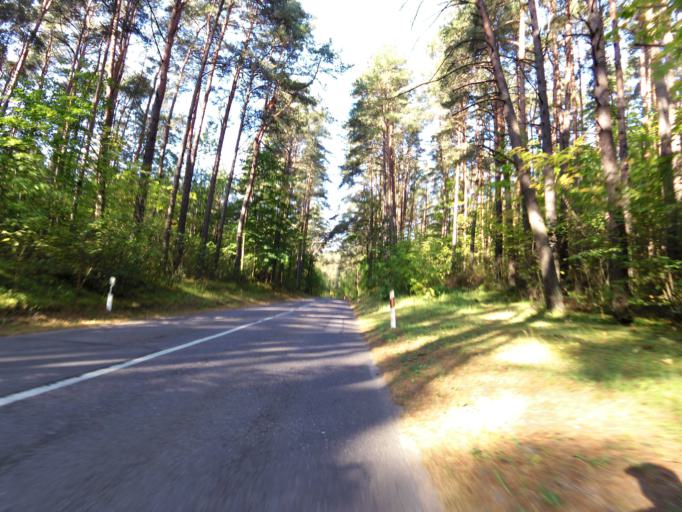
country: LT
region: Vilnius County
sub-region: Vilnius
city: Vilnius
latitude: 54.7323
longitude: 25.3031
